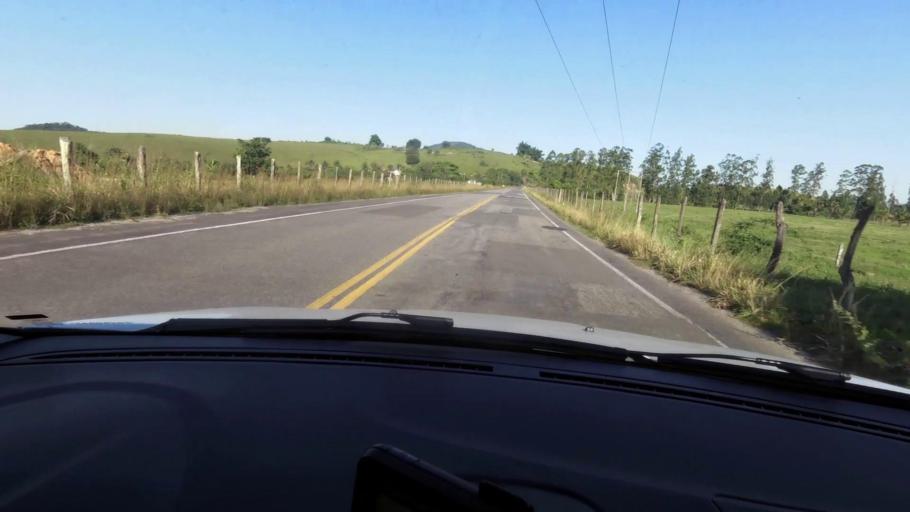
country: BR
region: Espirito Santo
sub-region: Alfredo Chaves
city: Alfredo Chaves
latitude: -20.7250
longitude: -40.6566
